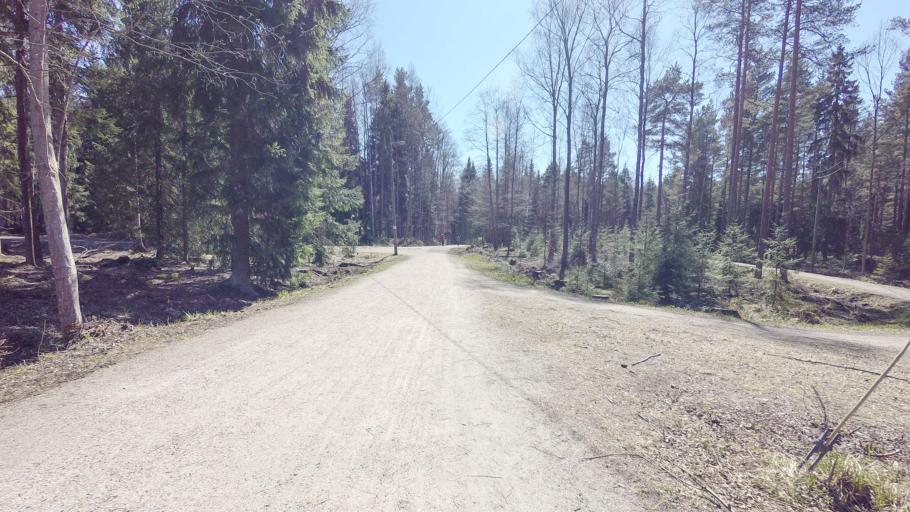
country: FI
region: Uusimaa
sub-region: Helsinki
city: Vantaa
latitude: 60.2289
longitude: 25.1460
